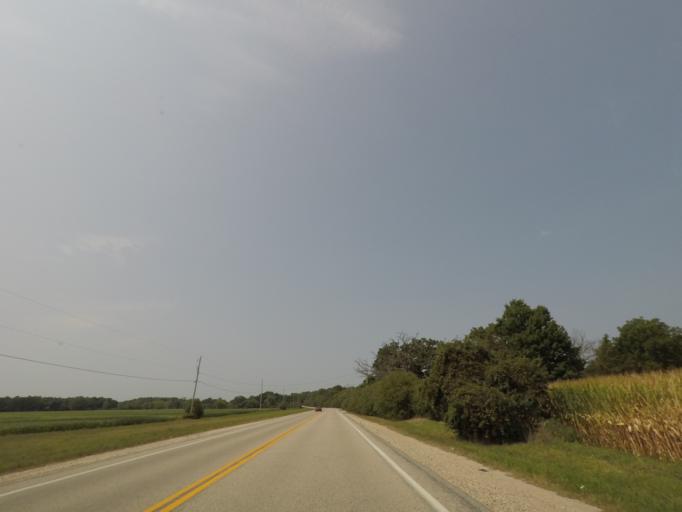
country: US
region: Wisconsin
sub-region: Waukesha County
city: Dousman
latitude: 43.0623
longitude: -88.4872
